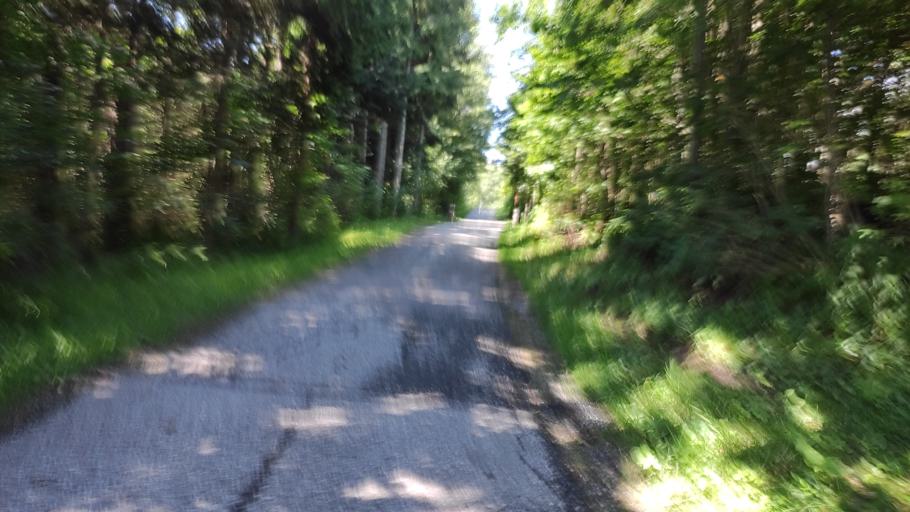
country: AT
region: Salzburg
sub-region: Politischer Bezirk Zell am See
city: Leogang
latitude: 47.4415
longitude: 12.7066
